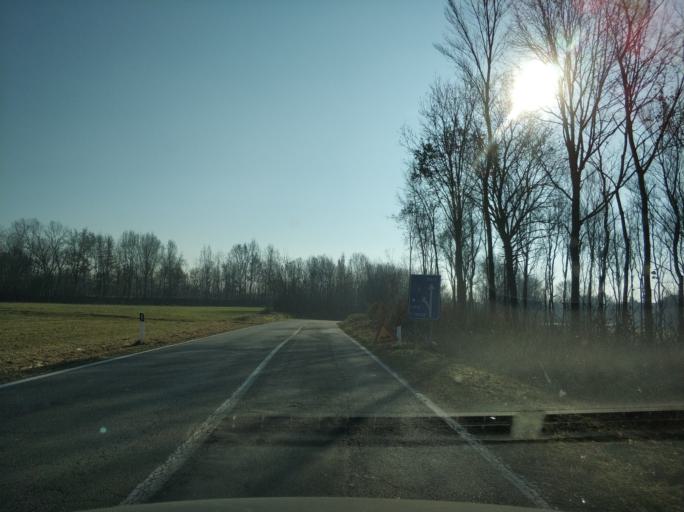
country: IT
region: Piedmont
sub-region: Provincia di Torino
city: Nole
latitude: 45.2604
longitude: 7.5823
